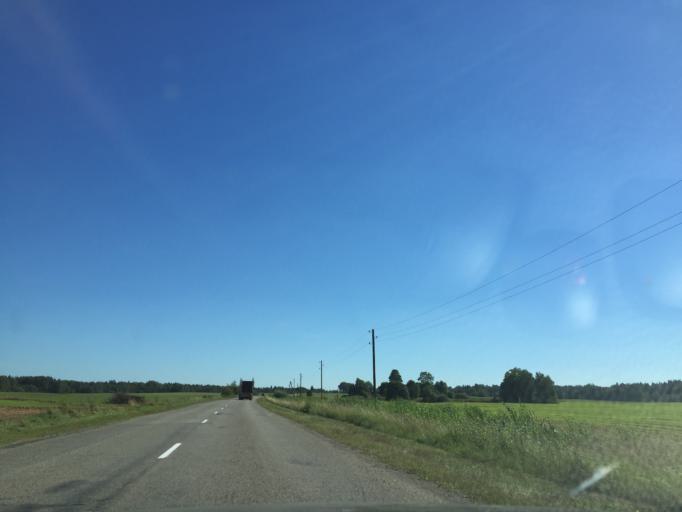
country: LV
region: Akniste
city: Akniste
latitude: 56.1070
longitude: 25.8540
